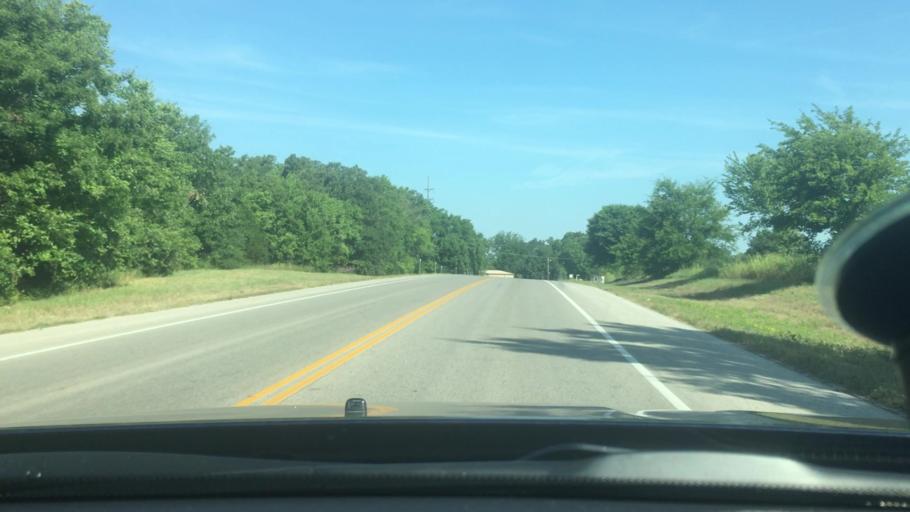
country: US
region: Oklahoma
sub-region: Garvin County
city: Pauls Valley
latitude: 34.6831
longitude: -97.2113
